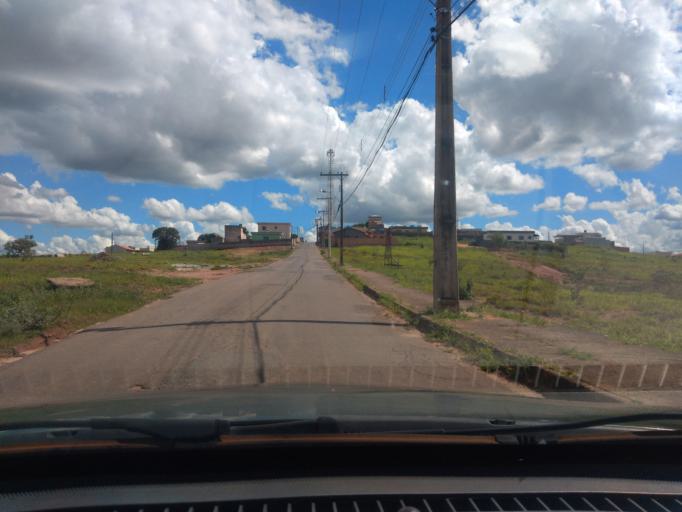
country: BR
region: Minas Gerais
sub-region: Tres Coracoes
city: Tres Coracoes
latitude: -21.6840
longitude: -45.2446
